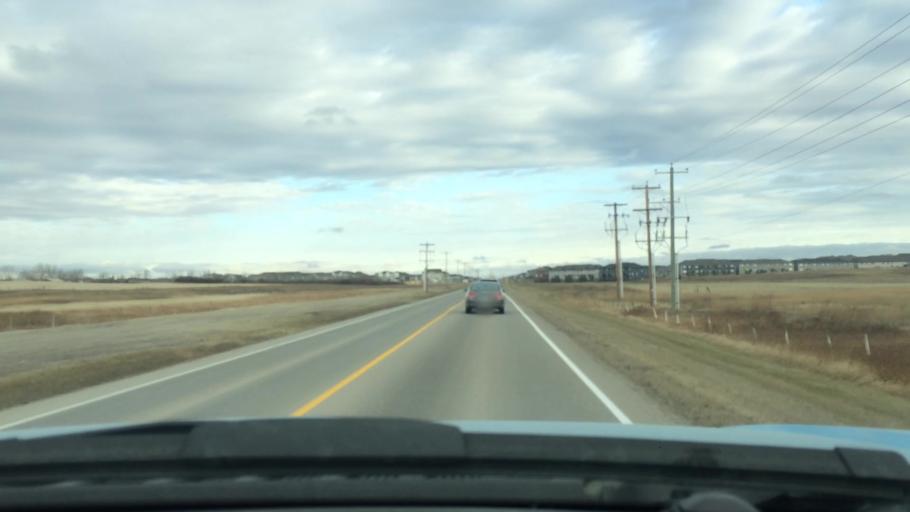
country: CA
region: Alberta
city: Airdrie
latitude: 51.2442
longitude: -114.0250
